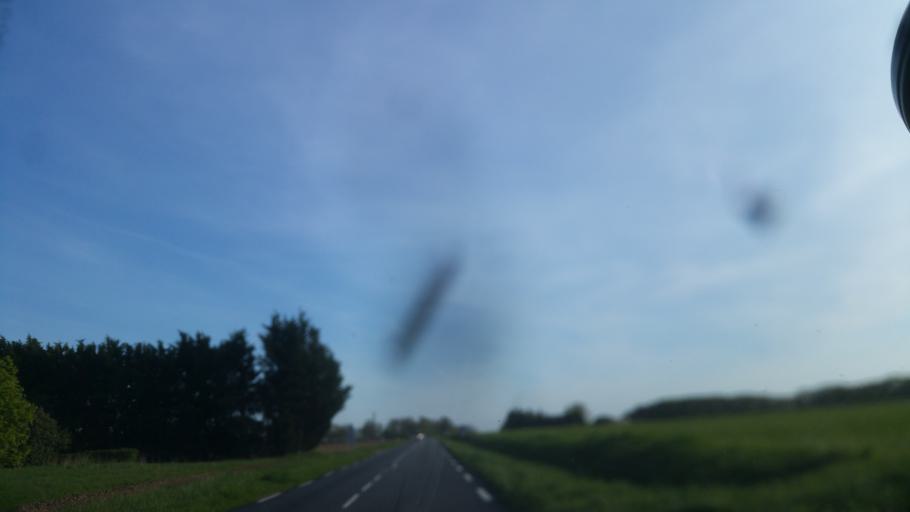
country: FR
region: Ile-de-France
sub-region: Departement de l'Essonne
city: Dourdan
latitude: 48.5436
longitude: 2.0181
